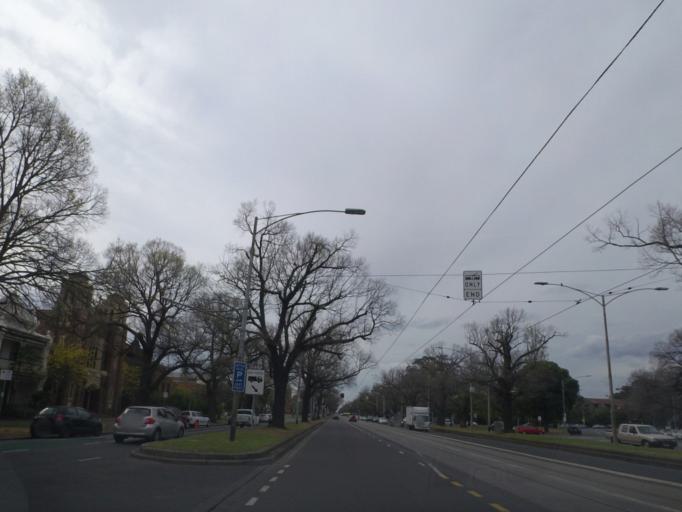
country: AU
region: Victoria
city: Carlton
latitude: -37.7938
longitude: 144.9582
